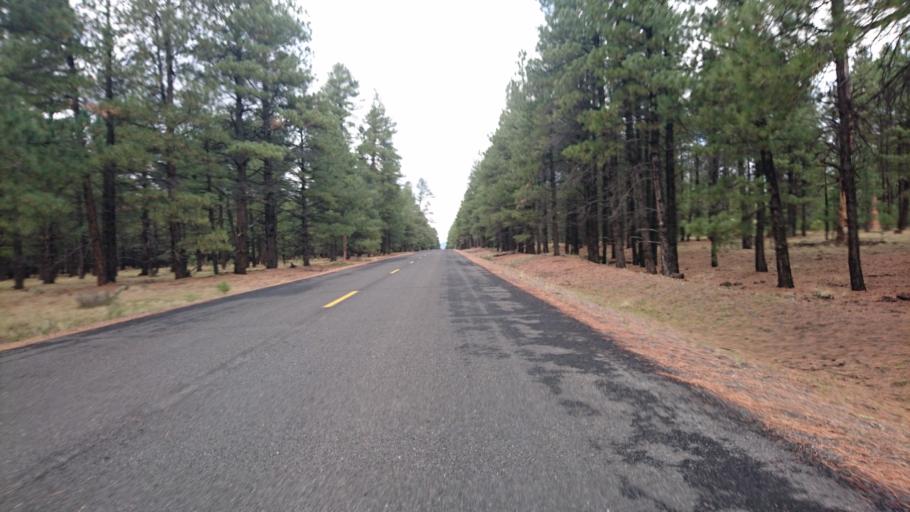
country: US
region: Arizona
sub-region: Coconino County
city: Parks
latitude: 35.2541
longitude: -111.8624
